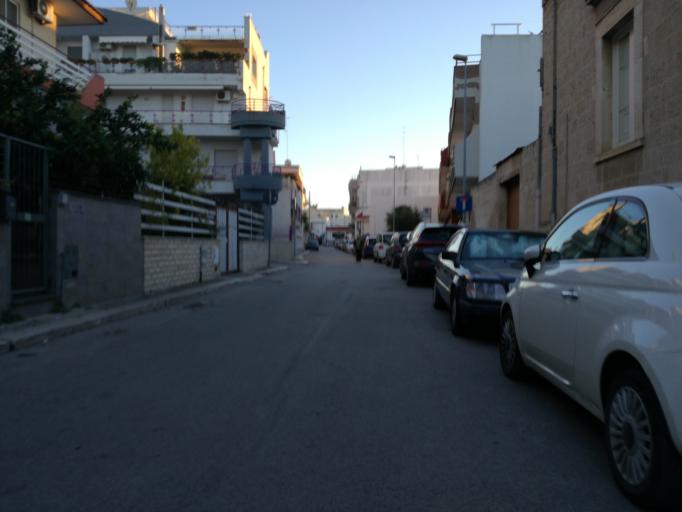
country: IT
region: Apulia
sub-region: Provincia di Bari
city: Adelfia
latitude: 41.0016
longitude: 16.8751
